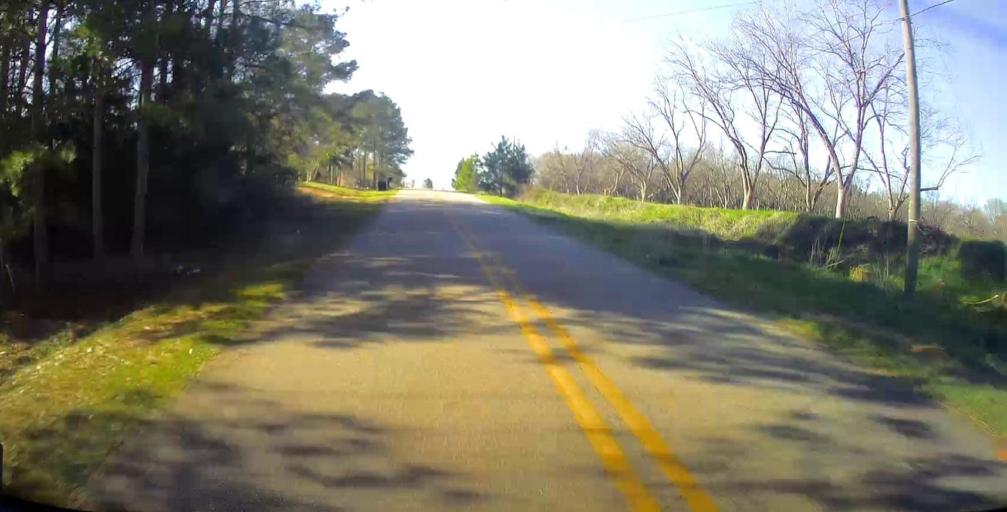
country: US
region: Georgia
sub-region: Macon County
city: Marshallville
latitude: 32.4659
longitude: -83.9473
